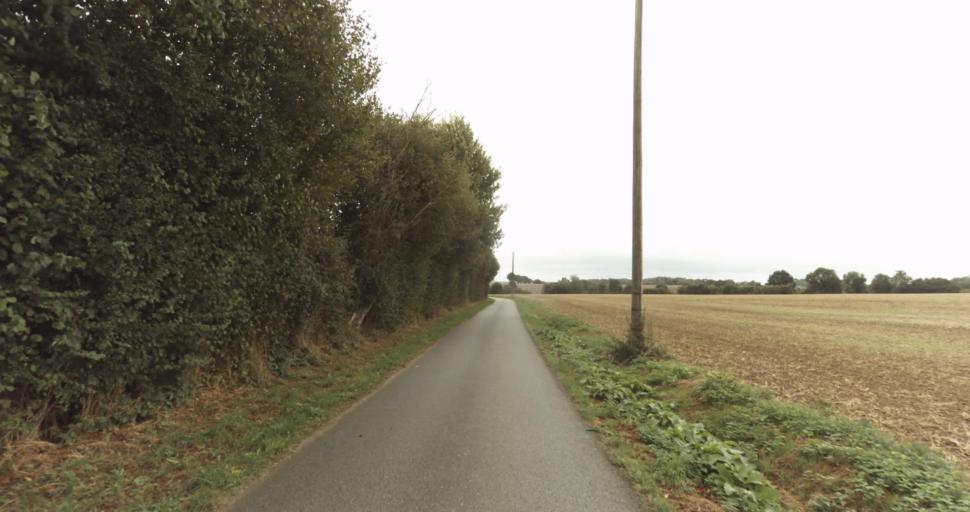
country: FR
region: Lower Normandy
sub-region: Departement de l'Orne
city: Sainte-Gauburge-Sainte-Colombe
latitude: 48.7411
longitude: 0.4536
